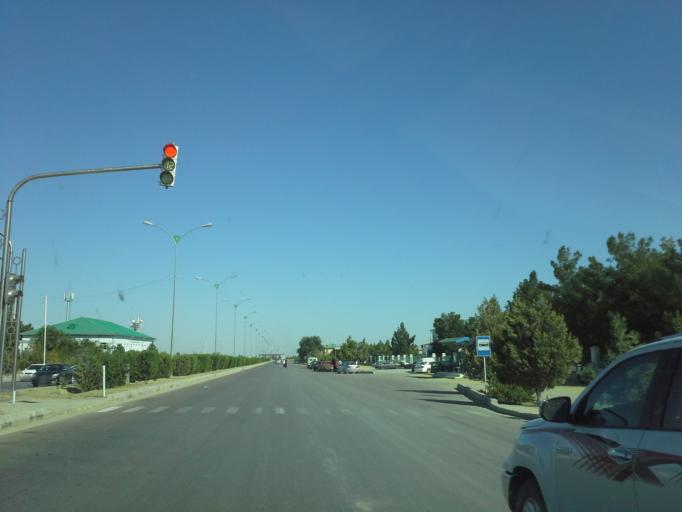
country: TM
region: Ahal
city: Baharly
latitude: 38.4265
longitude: 57.4287
